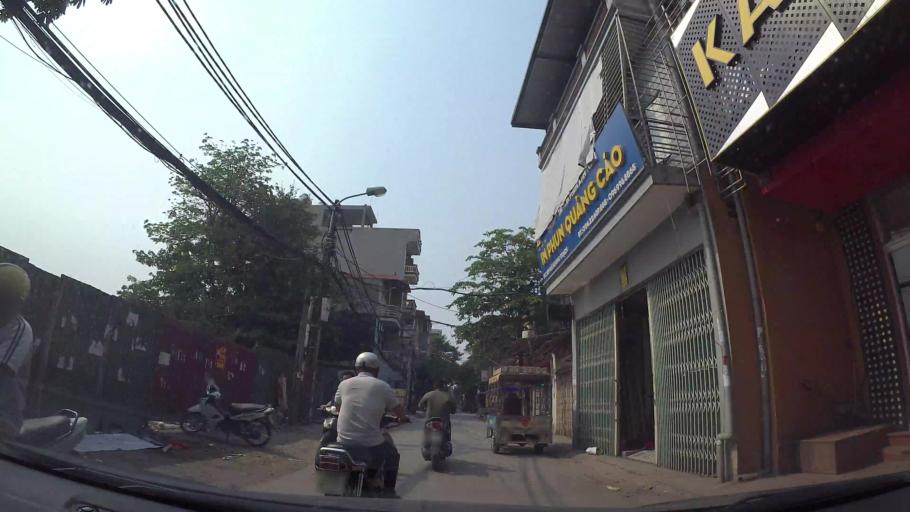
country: VN
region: Ha Noi
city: Thanh Xuan
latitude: 20.9868
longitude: 105.8189
